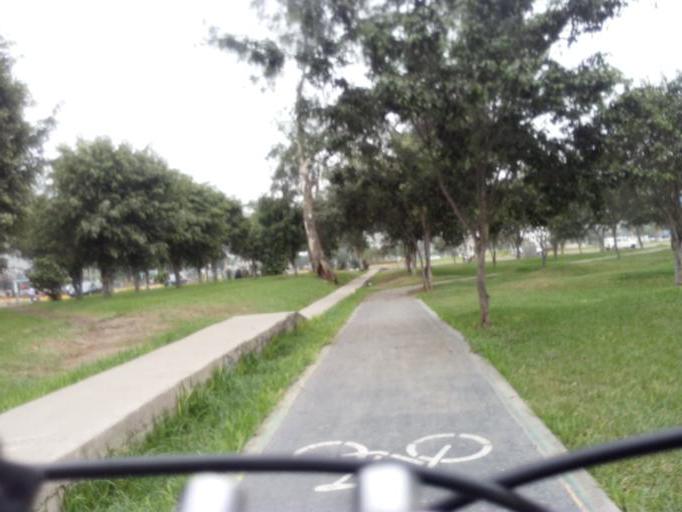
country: PE
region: Lima
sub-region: Lima
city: La Molina
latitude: -12.0636
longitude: -76.9406
